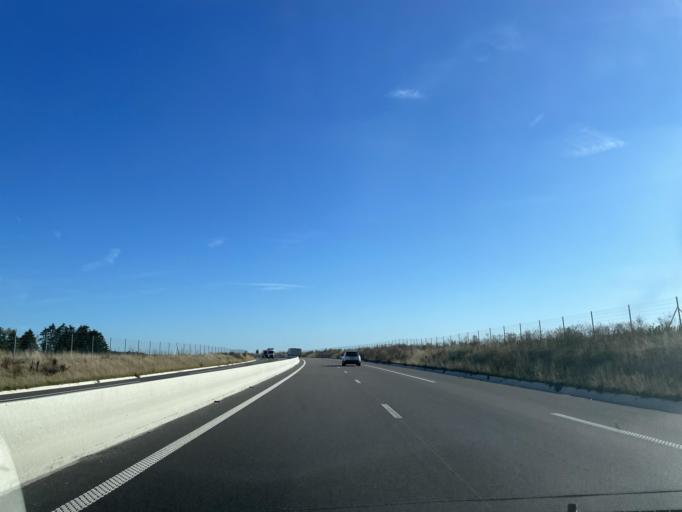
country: FR
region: Picardie
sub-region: Departement de l'Oise
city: Peroy-les-Gombries
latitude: 49.1563
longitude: 2.8504
